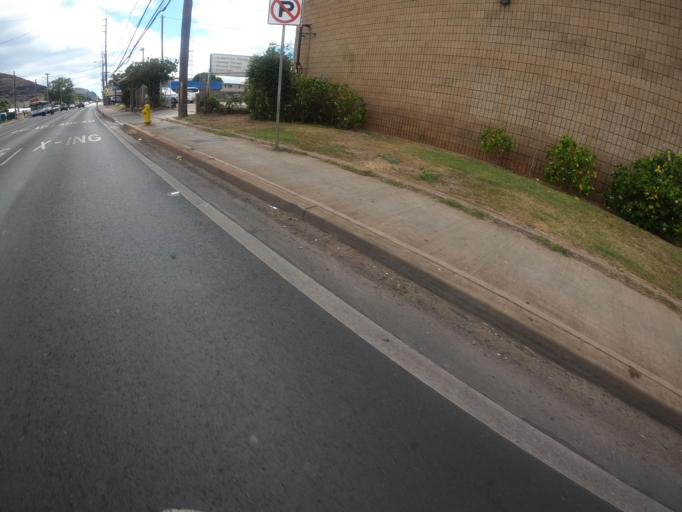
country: US
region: Hawaii
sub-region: Honolulu County
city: Waianae
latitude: 21.4450
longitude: -158.1879
